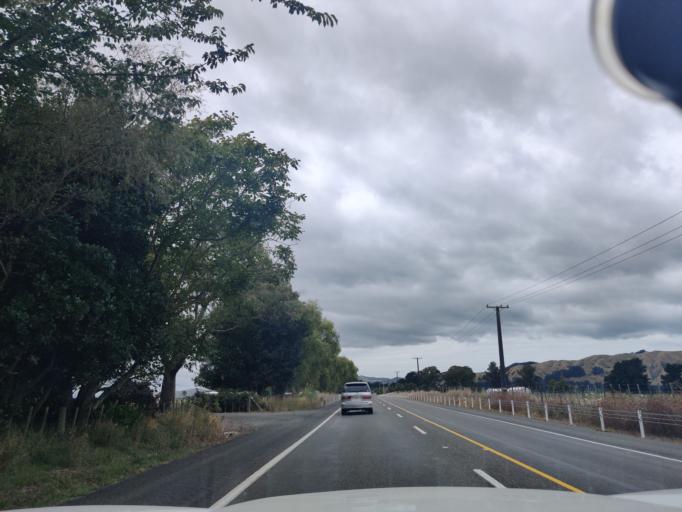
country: NZ
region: Manawatu-Wanganui
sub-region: Horowhenua District
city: Levin
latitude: -40.5782
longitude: 175.3678
